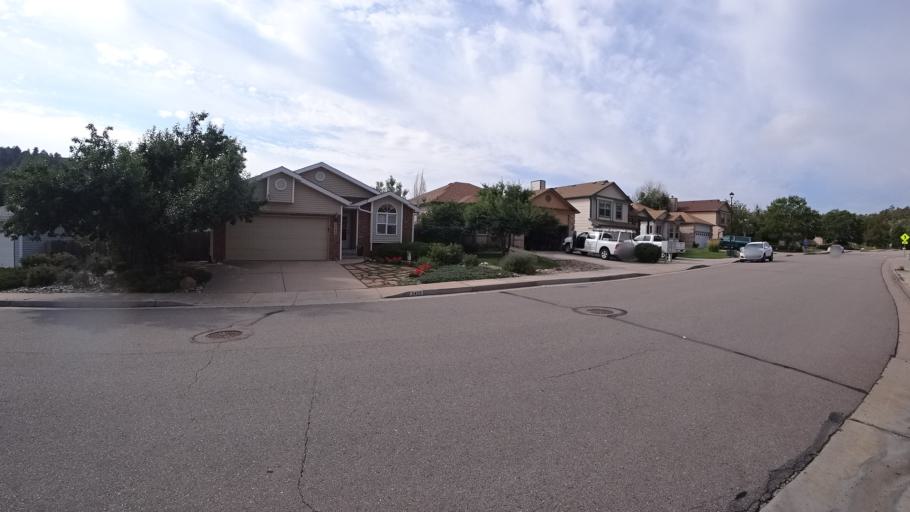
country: US
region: Colorado
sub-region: El Paso County
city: Colorado Springs
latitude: 38.8953
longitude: -104.7866
